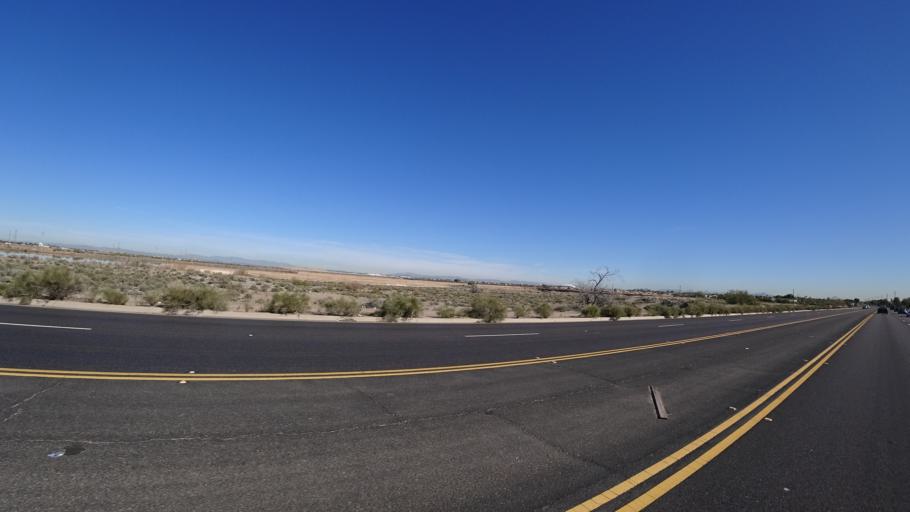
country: US
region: Arizona
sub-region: Maricopa County
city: Litchfield Park
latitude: 33.4931
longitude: -112.3117
